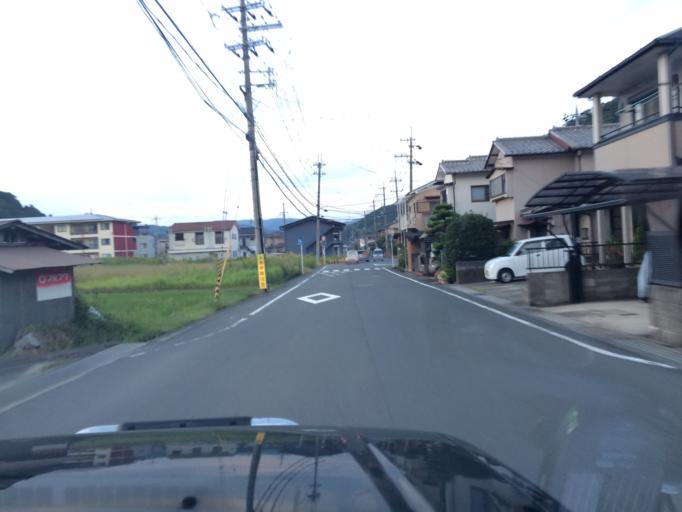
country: JP
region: Kyoto
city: Kameoka
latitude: 35.0952
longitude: 135.4748
